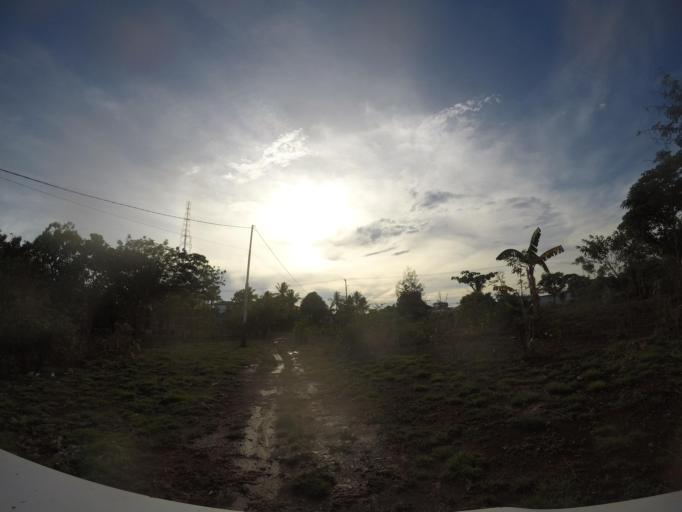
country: TL
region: Baucau
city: Baucau
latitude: -8.4874
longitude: 126.4529
